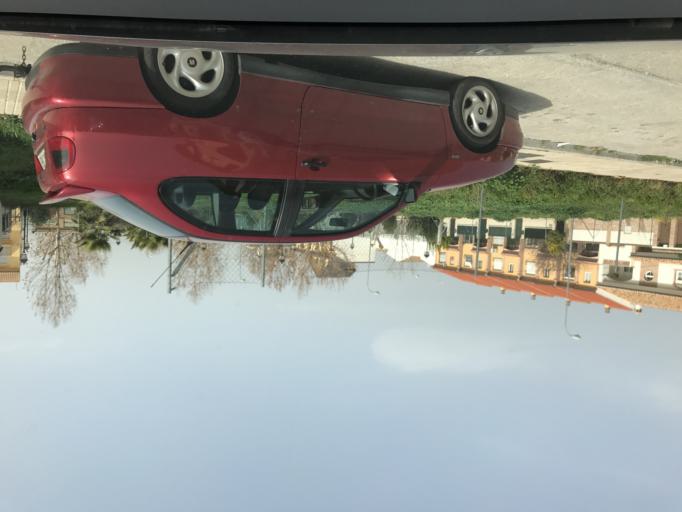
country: ES
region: Andalusia
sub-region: Provincia de Granada
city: Atarfe
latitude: 37.1892
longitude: -3.7092
